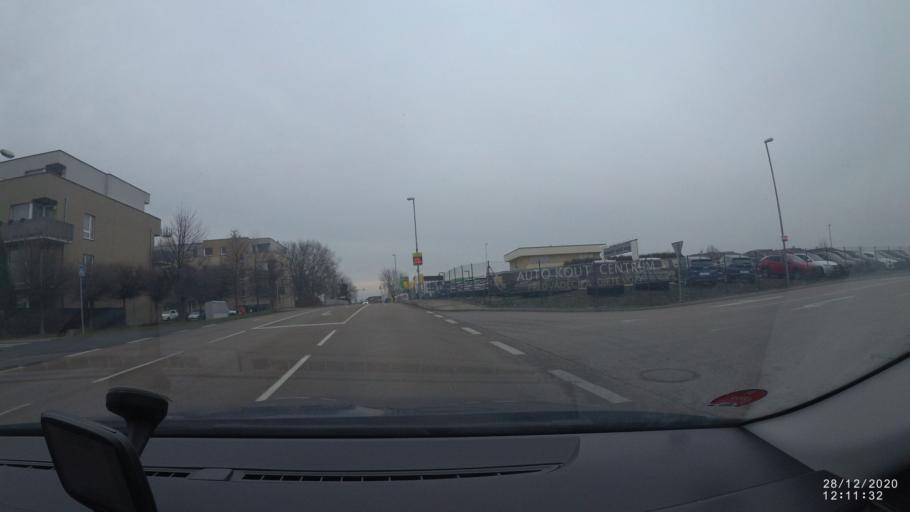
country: CZ
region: Central Bohemia
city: Brandys nad Labem-Stara Boleslav
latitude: 50.1737
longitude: 14.6467
